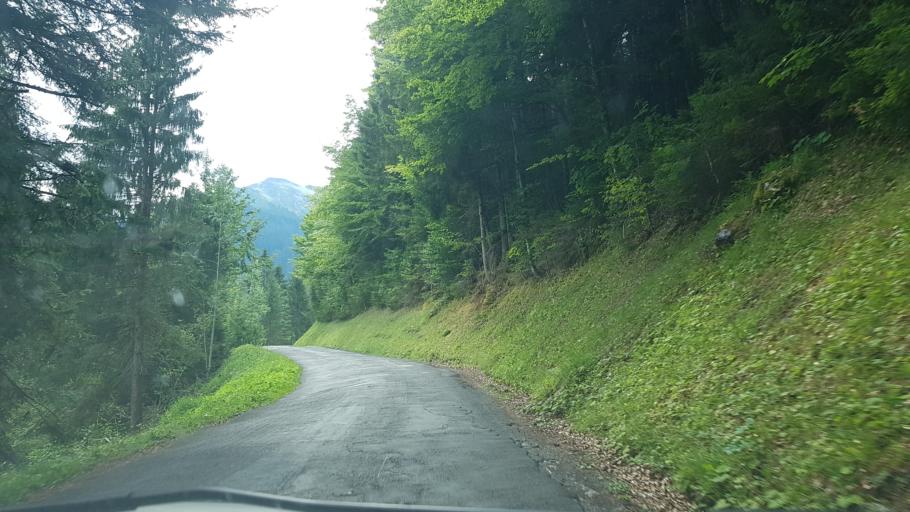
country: FR
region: Rhone-Alpes
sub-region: Departement de la Haute-Savoie
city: Samoens
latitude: 46.0331
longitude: 6.7690
